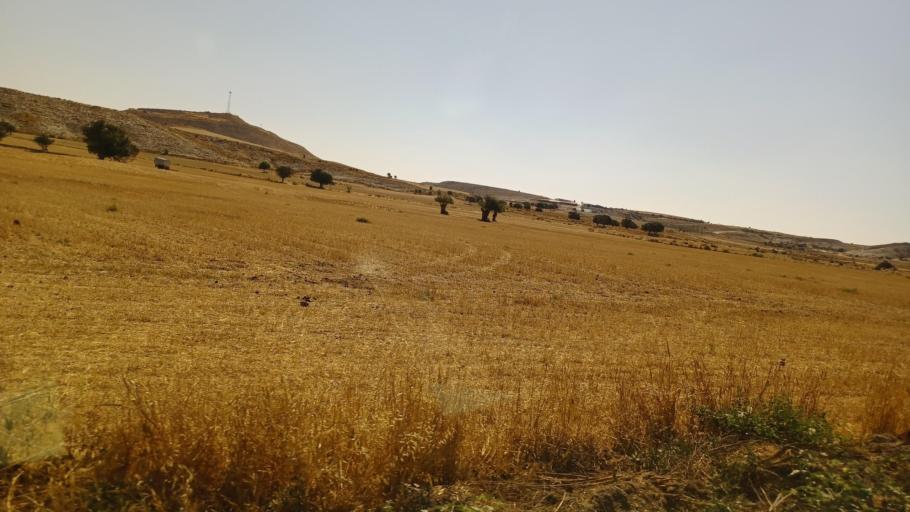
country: CY
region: Larnaka
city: Athienou
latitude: 35.0323
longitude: 33.5121
